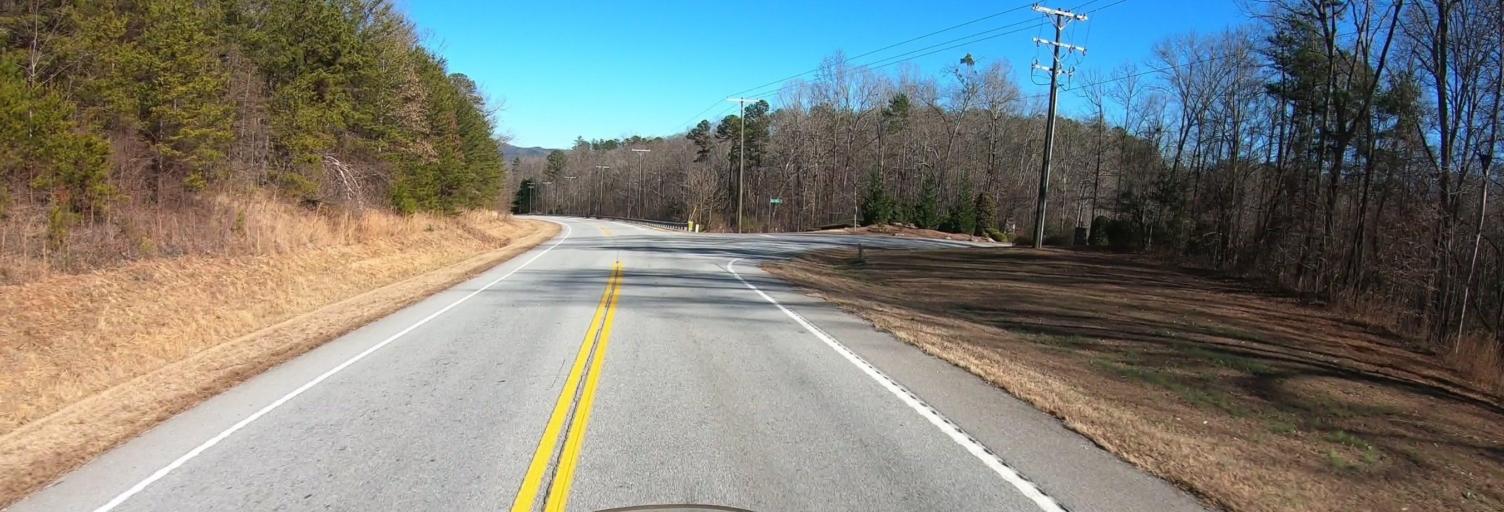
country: US
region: South Carolina
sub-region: Oconee County
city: Walhalla
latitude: 34.9149
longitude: -82.9194
